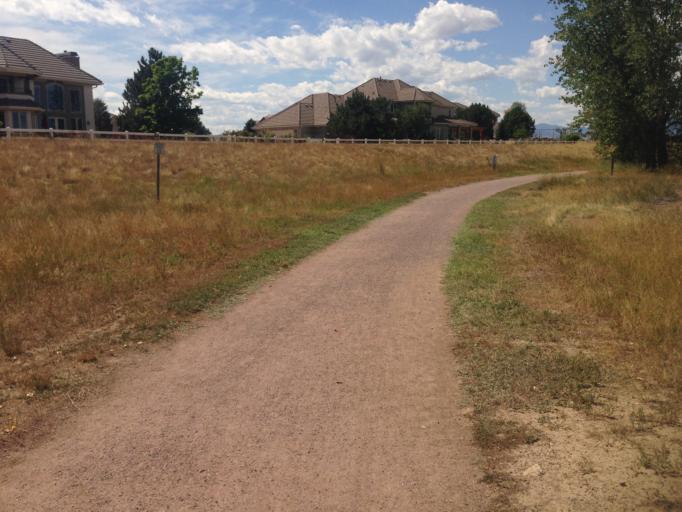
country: US
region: Colorado
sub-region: Adams County
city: Northglenn
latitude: 39.9527
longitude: -105.0082
